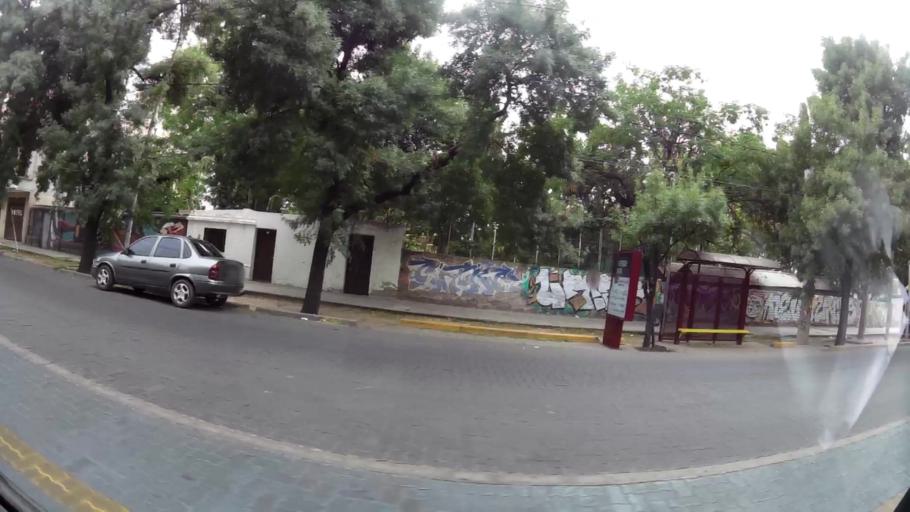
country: AR
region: Mendoza
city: Mendoza
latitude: -32.8843
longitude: -68.8491
